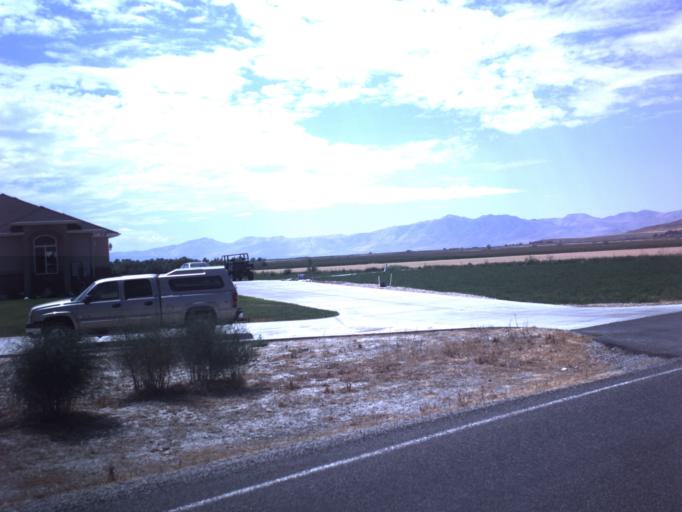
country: US
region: Utah
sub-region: Box Elder County
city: Tremonton
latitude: 41.6509
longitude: -112.2968
